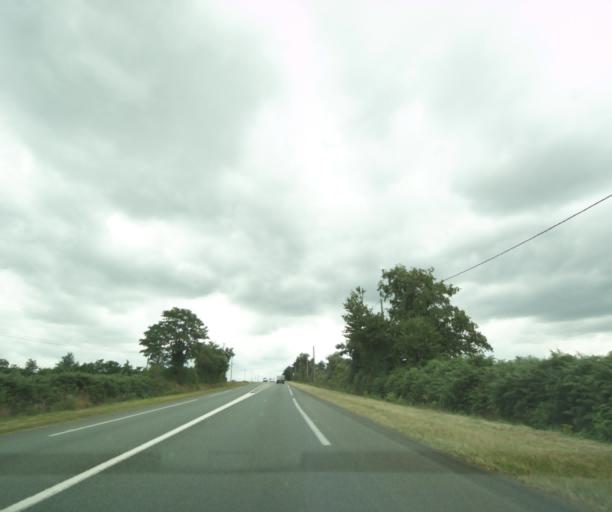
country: FR
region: Pays de la Loire
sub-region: Departement de Maine-et-Loire
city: Durtal
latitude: 47.6530
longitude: -0.2594
